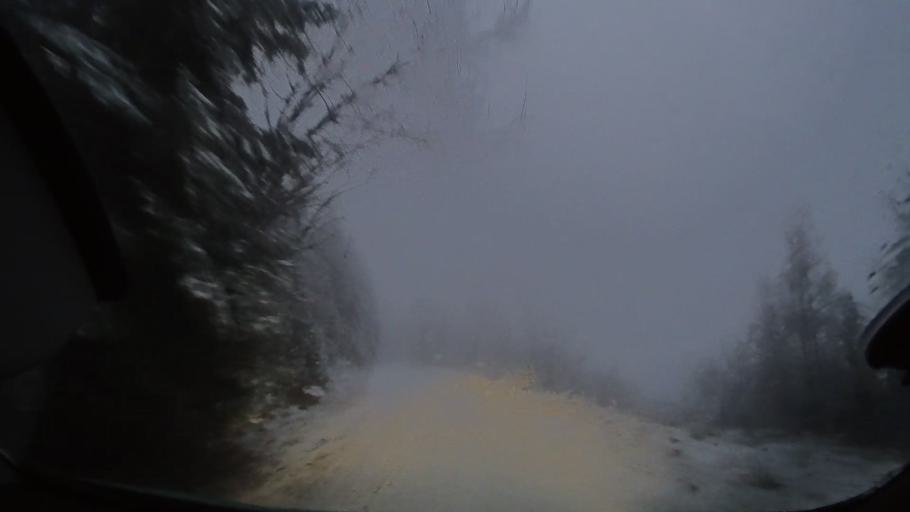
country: RO
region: Alba
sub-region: Comuna Avram Iancu
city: Avram Iancu
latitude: 46.3114
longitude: 22.8098
